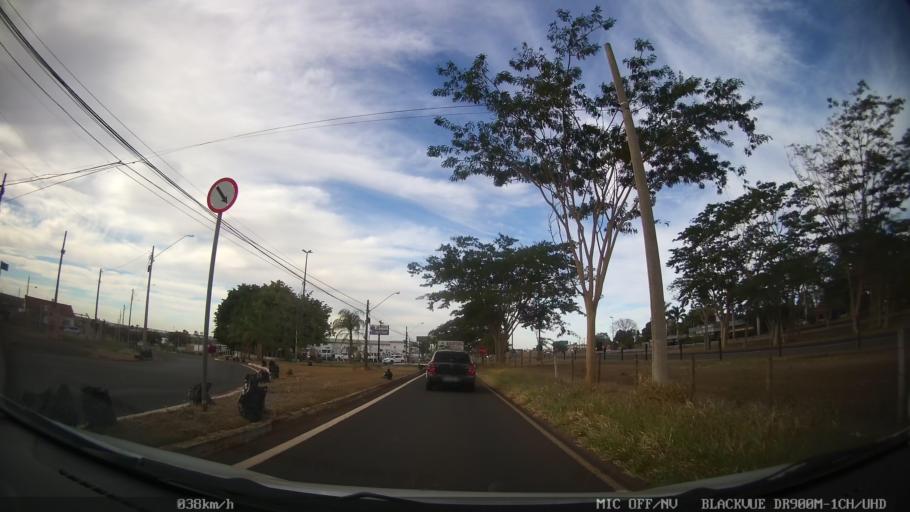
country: BR
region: Sao Paulo
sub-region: Catanduva
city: Catanduva
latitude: -21.1507
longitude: -48.9980
